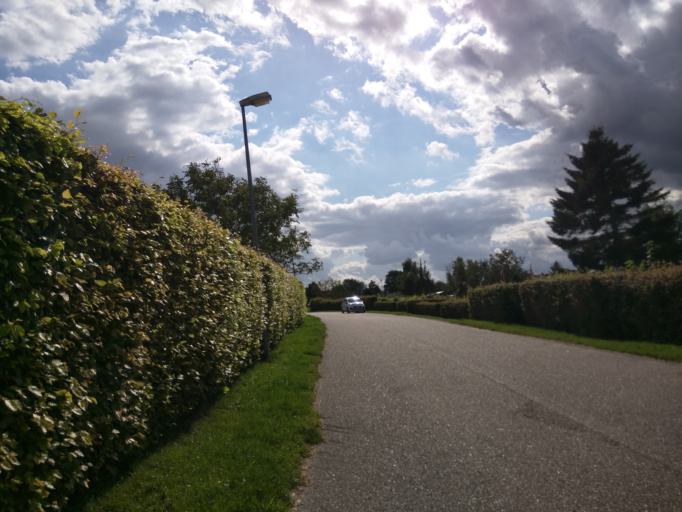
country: DK
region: Central Jutland
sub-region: Viborg Kommune
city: Viborg
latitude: 56.4570
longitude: 9.3962
